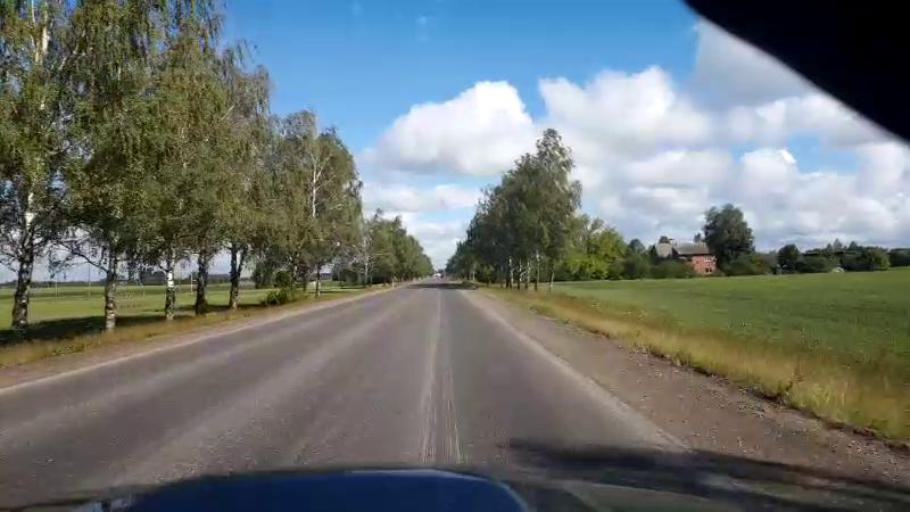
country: LV
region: Bauskas Rajons
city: Bauska
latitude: 56.3541
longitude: 24.2859
